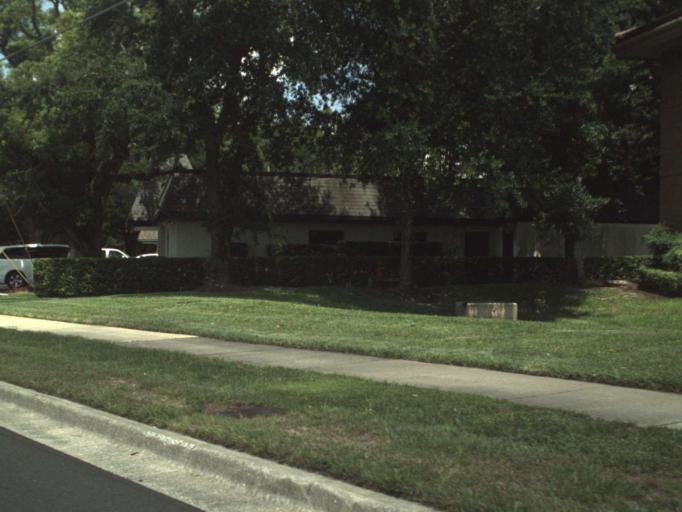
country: US
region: Florida
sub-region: Seminole County
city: Altamonte Springs
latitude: 28.6974
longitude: -81.3770
